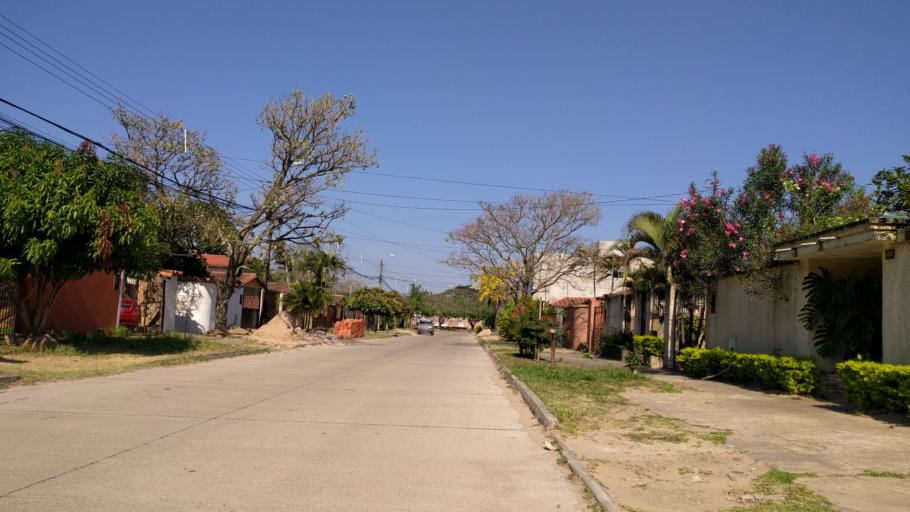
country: BO
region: Santa Cruz
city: Santa Cruz de la Sierra
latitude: -17.8096
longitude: -63.2254
